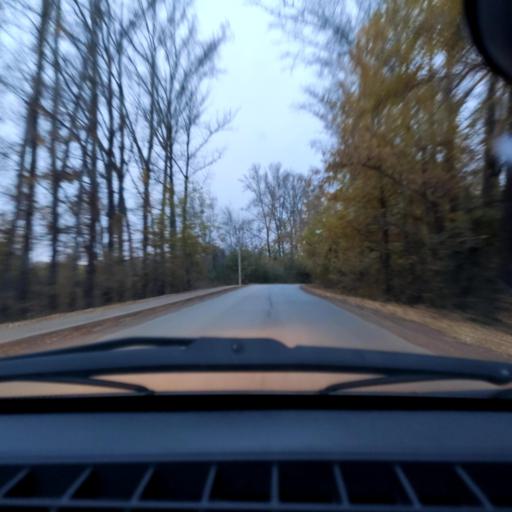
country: RU
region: Bashkortostan
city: Ufa
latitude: 54.6929
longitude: 55.9664
